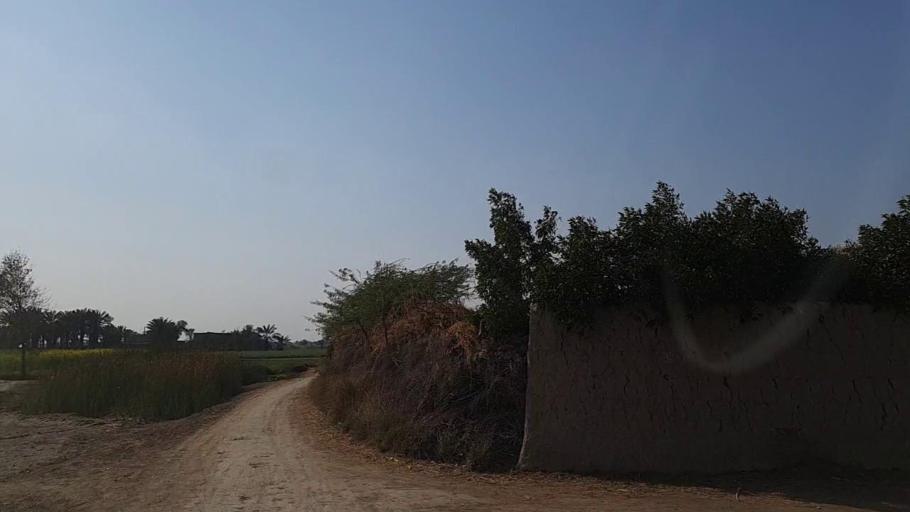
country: PK
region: Sindh
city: Daur
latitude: 26.4368
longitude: 68.2606
